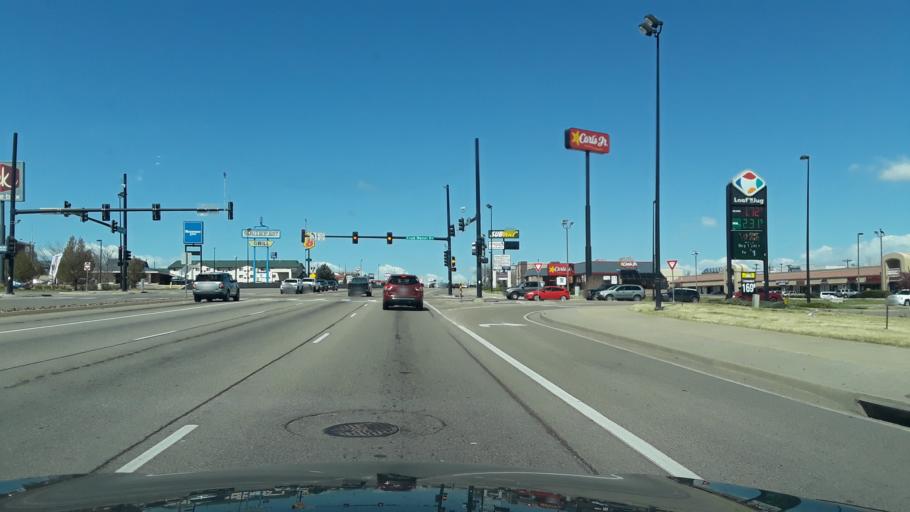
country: US
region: Colorado
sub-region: Pueblo County
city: Pueblo
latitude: 38.3081
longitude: -104.6197
